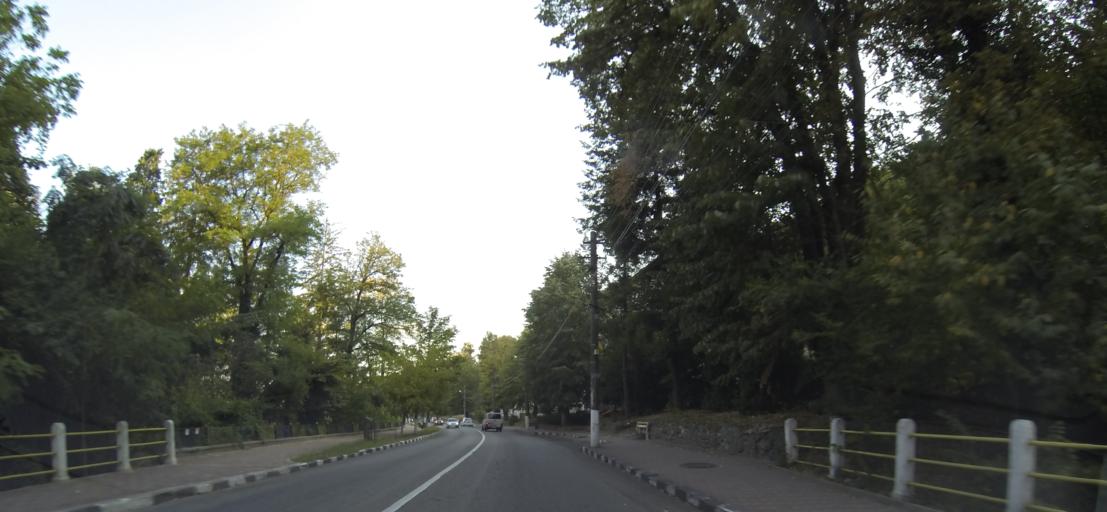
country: RO
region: Valcea
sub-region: Oras Calimanesti
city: Jiblea Veche
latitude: 45.2514
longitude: 24.3364
